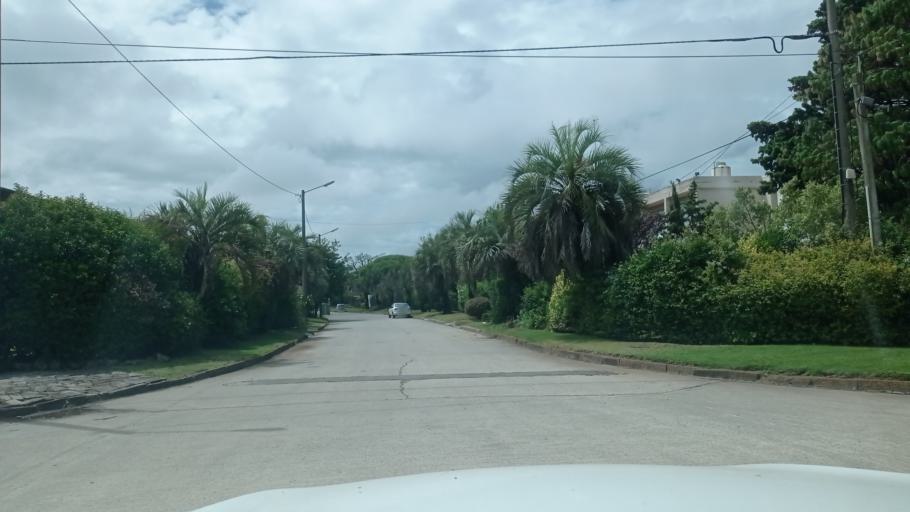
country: UY
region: Canelones
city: Barra de Carrasco
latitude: -34.8854
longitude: -56.0498
